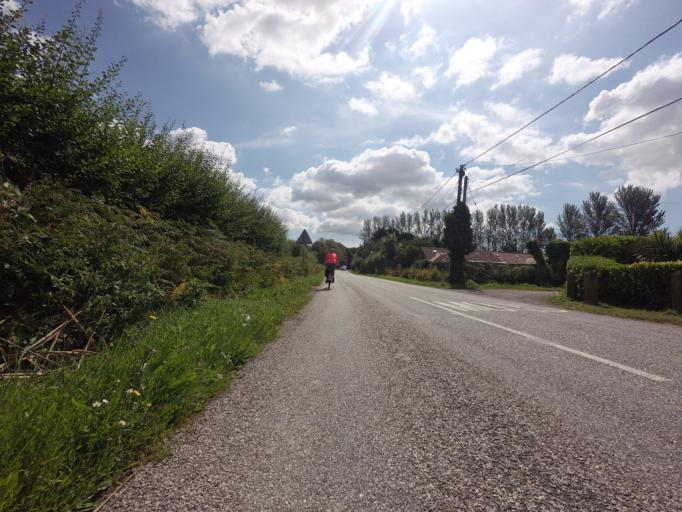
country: GB
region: England
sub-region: Kent
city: Tenterden
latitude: 51.0726
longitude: 0.7402
